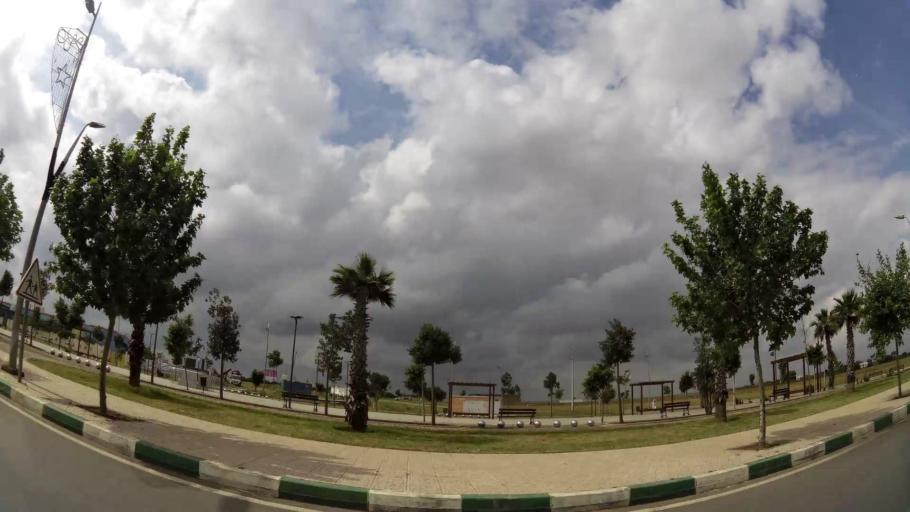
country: MA
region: Rabat-Sale-Zemmour-Zaer
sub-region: Khemisset
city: Tiflet
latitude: 33.8944
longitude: -6.3363
